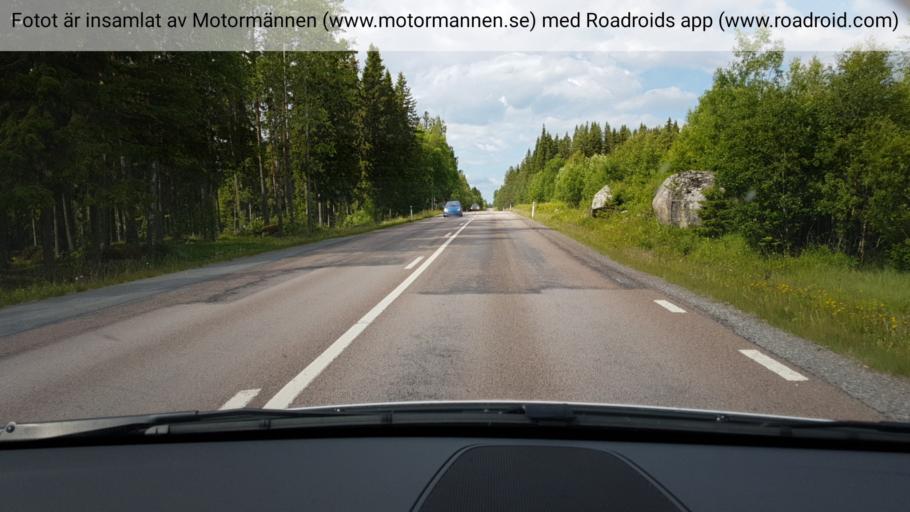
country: SE
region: Jaemtland
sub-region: OEstersunds Kommun
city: Brunflo
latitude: 63.0342
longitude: 14.8987
